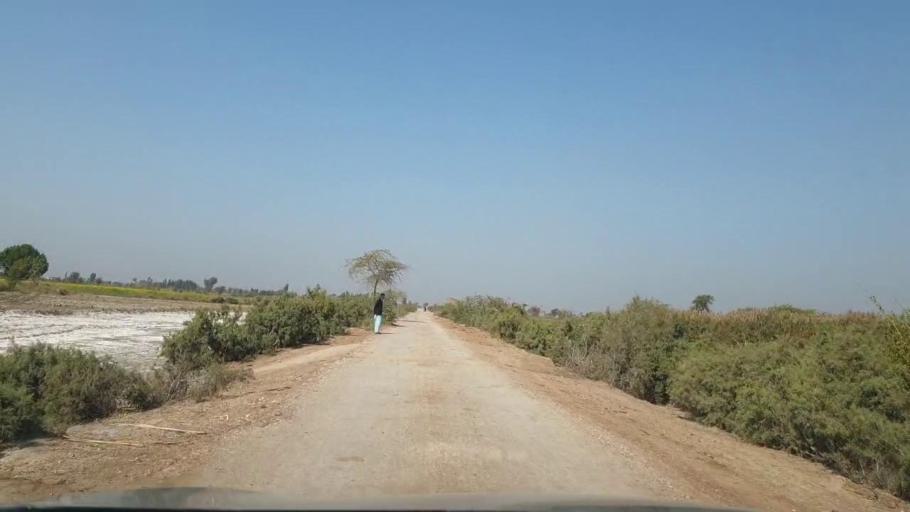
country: PK
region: Sindh
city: Berani
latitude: 25.6804
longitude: 68.8948
